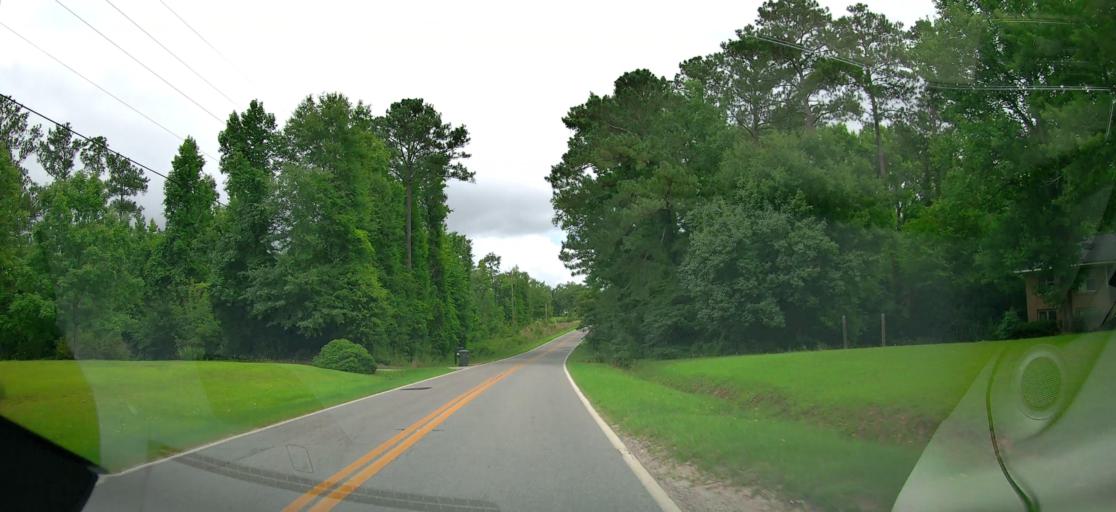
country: US
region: Georgia
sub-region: Bibb County
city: West Point
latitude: 32.7416
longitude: -83.7657
